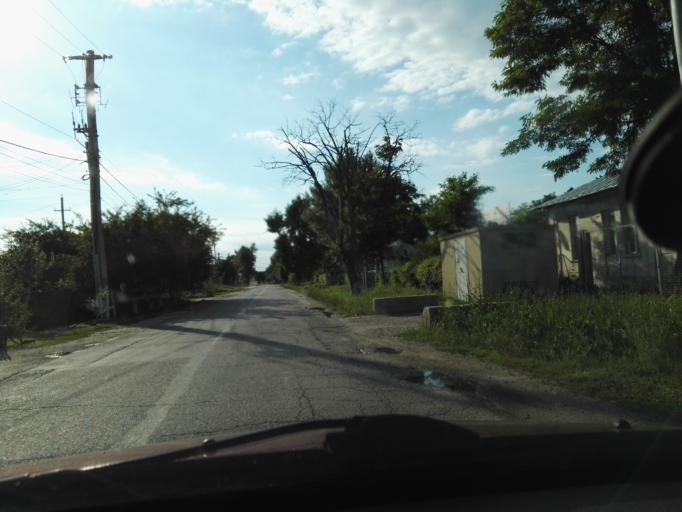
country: RO
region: Ilfov
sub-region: Comuna Copaceni
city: Copaceni
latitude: 44.2423
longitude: 26.1031
